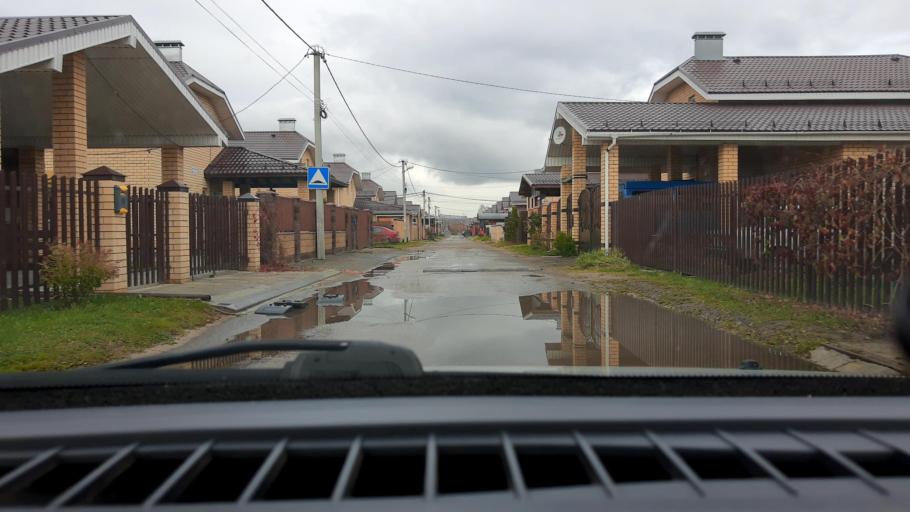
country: RU
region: Nizjnij Novgorod
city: Afonino
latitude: 56.2019
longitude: 44.1283
